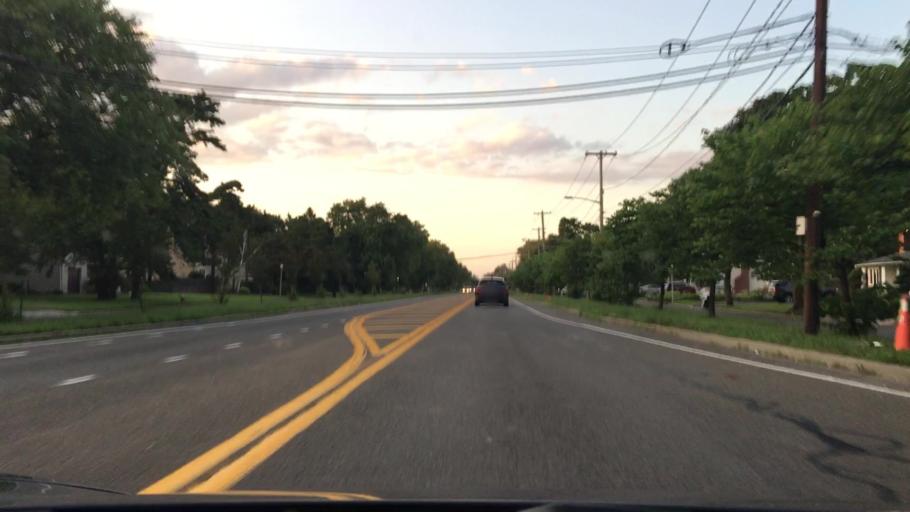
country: US
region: New York
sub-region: Suffolk County
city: Dix Hills
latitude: 40.7961
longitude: -73.2973
